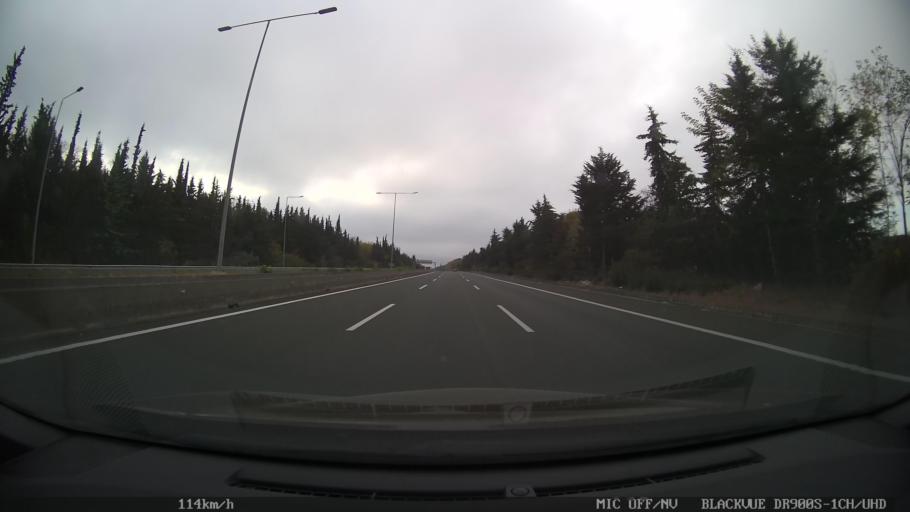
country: GR
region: Central Macedonia
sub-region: Nomos Pierias
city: Makrygialos
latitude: 40.4540
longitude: 22.5796
